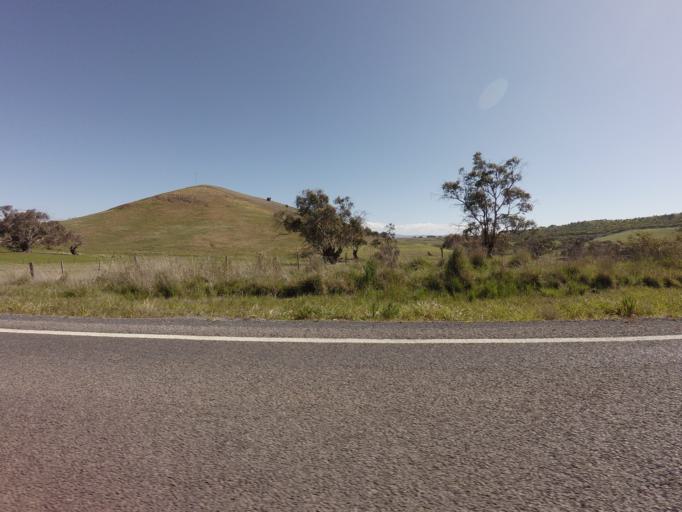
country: AU
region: Tasmania
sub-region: Derwent Valley
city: New Norfolk
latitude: -42.5716
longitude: 146.8816
